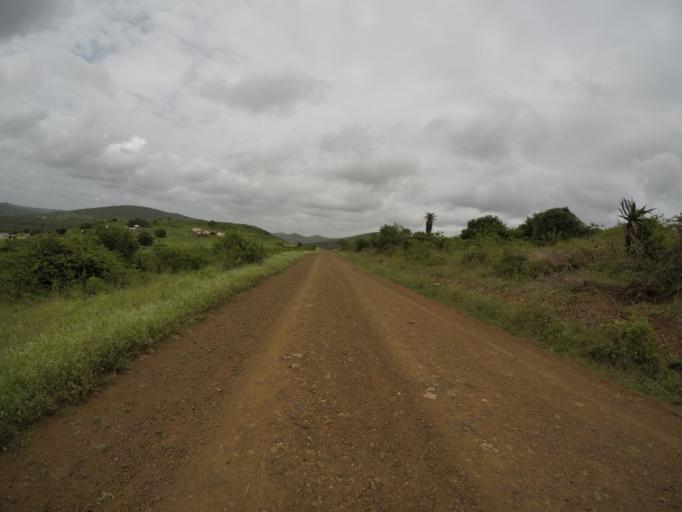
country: ZA
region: KwaZulu-Natal
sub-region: uThungulu District Municipality
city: Empangeni
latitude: -28.6253
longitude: 31.8892
